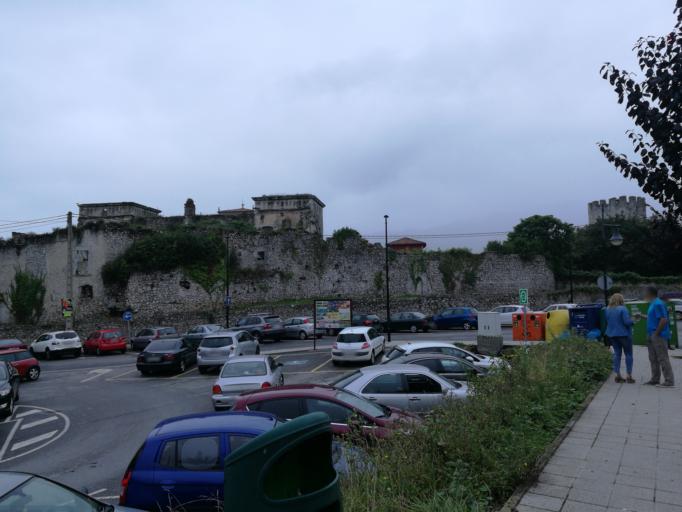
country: ES
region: Asturias
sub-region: Province of Asturias
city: Llanes
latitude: 43.4223
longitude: -4.7548
